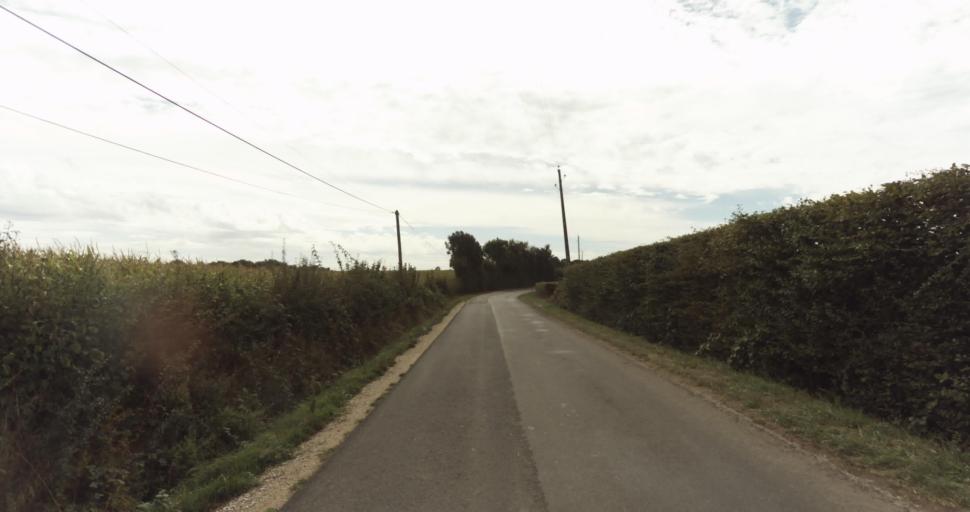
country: FR
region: Lower Normandy
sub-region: Departement du Calvados
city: La Vespiere
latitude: 48.9416
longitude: 0.3513
